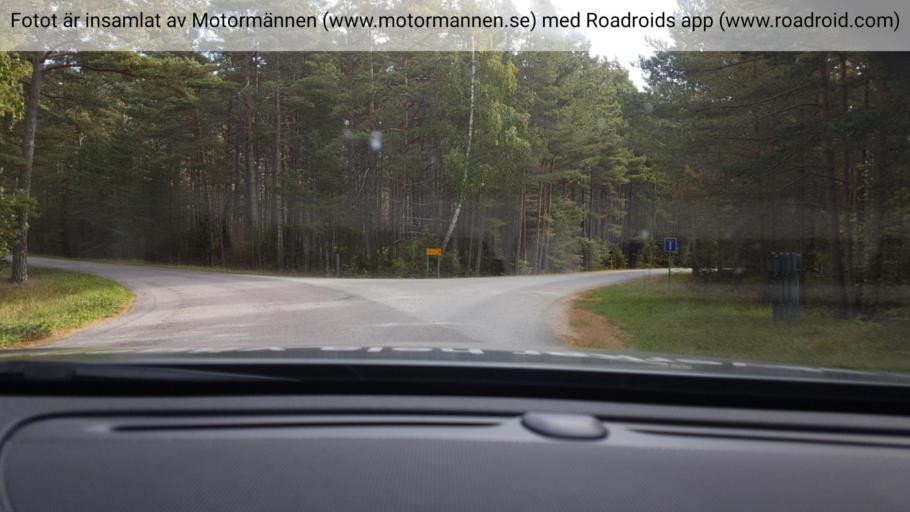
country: SE
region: Gotland
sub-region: Gotland
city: Slite
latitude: 57.9551
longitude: 19.2858
